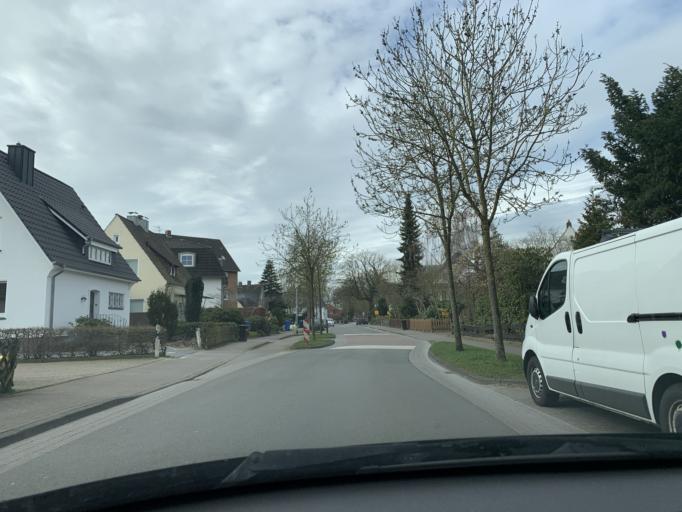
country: DE
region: Lower Saxony
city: Oldenburg
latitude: 53.1260
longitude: 8.2023
